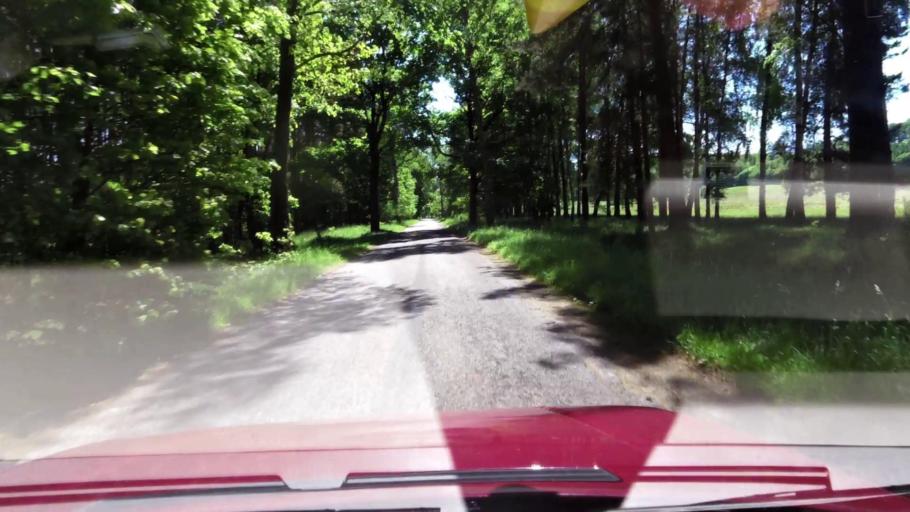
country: PL
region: West Pomeranian Voivodeship
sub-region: Powiat koszalinski
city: Bobolice
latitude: 54.0426
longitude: 16.5951
